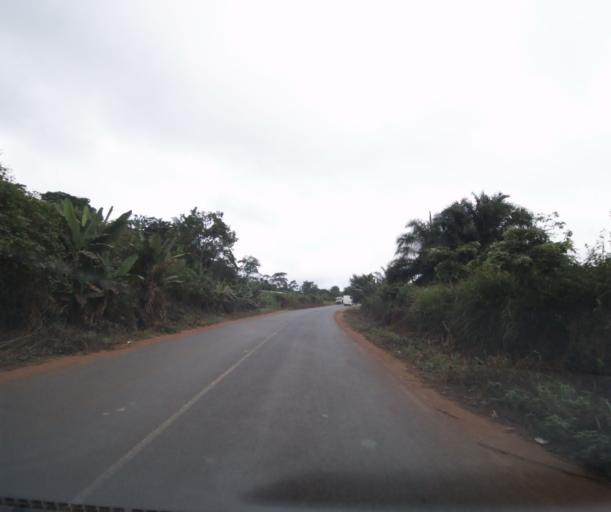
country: CM
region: Centre
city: Mbankomo
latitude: 3.7872
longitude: 11.4287
